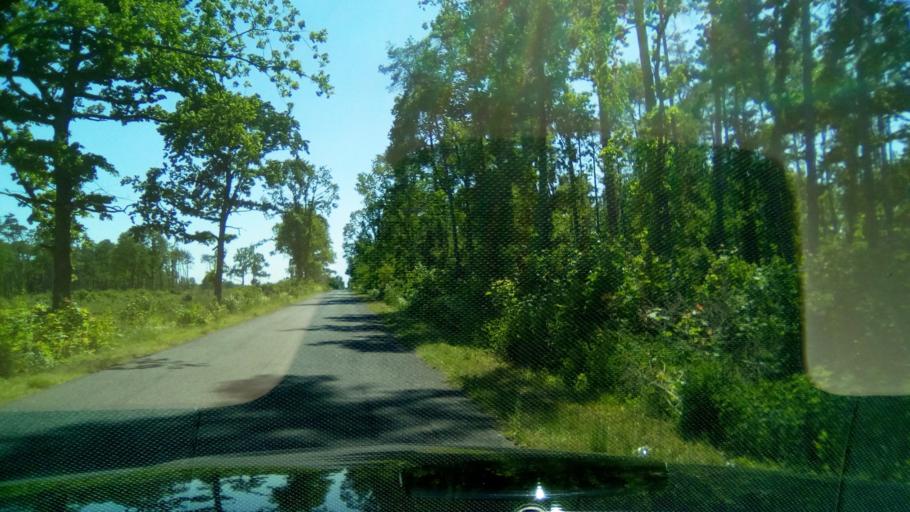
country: PL
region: Greater Poland Voivodeship
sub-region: Powiat gnieznienski
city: Gniezno
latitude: 52.4848
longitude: 17.5727
